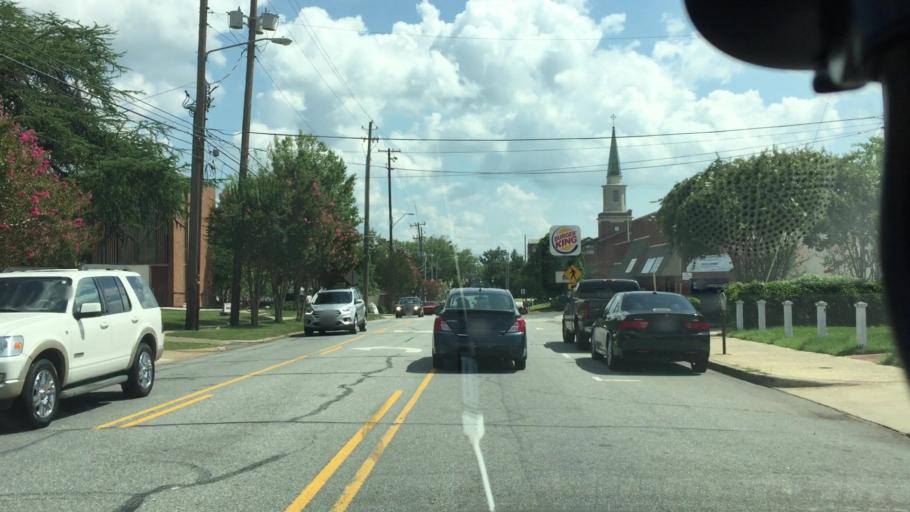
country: US
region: Alabama
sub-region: Lee County
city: Auburn
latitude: 32.6060
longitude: -85.4799
